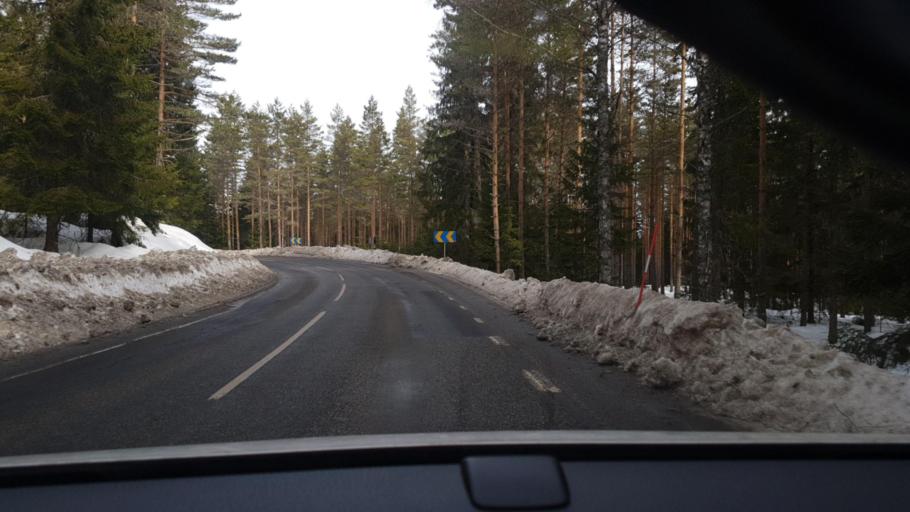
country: SE
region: Vaermland
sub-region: Eda Kommun
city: Amotfors
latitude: 59.6048
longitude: 12.3226
